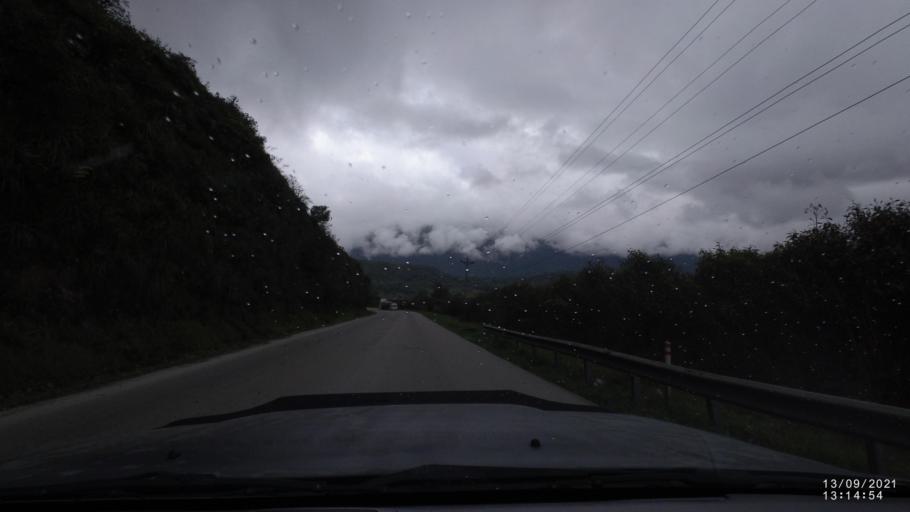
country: BO
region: Cochabamba
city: Colomi
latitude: -17.1945
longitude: -65.8528
